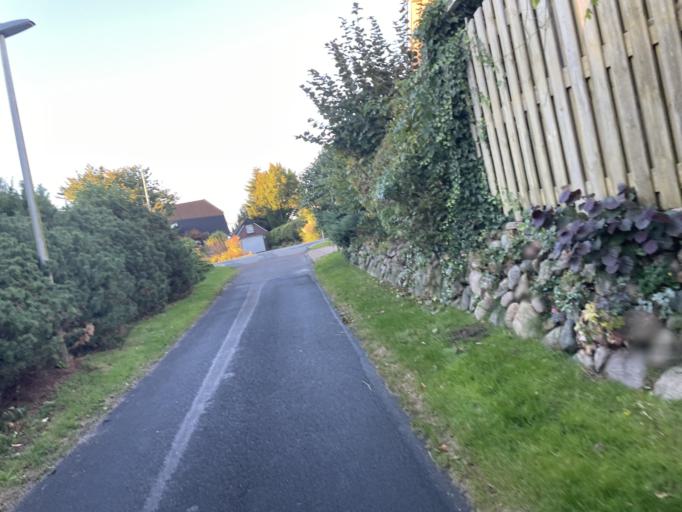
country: DE
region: Schleswig-Holstein
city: Mildstedt
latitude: 54.4803
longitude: 9.1031
